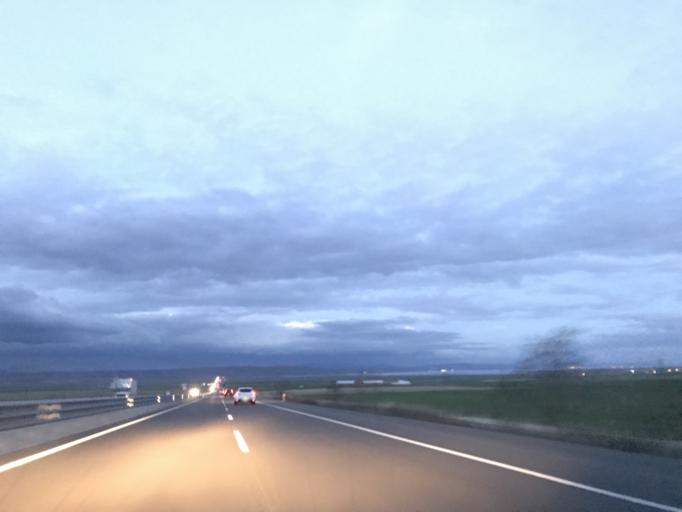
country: TR
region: Konya
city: Kulu
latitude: 39.1553
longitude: 33.2172
